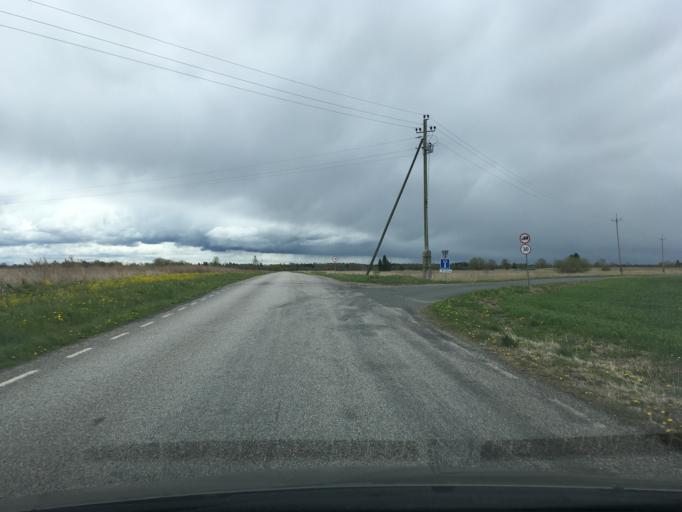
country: EE
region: Harju
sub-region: Rae vald
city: Vaida
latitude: 59.3579
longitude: 24.9773
